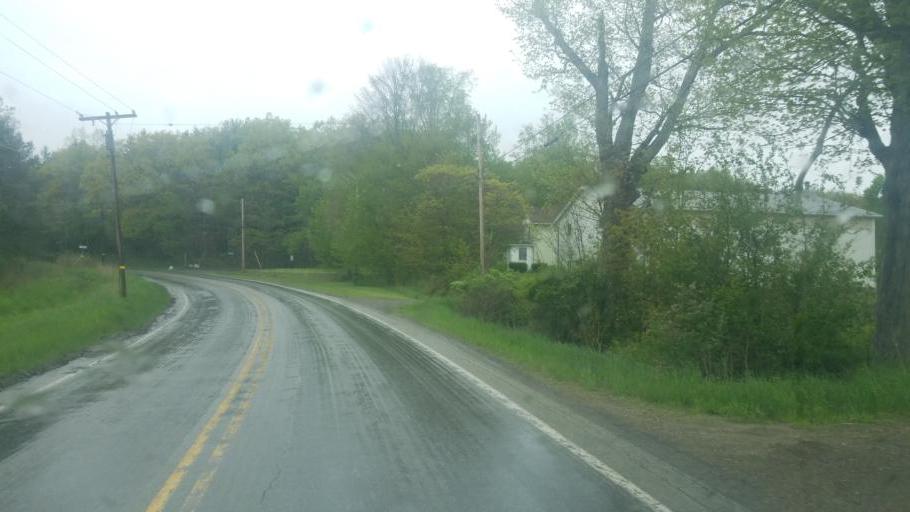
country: US
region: Pennsylvania
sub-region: Forest County
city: Tionesta
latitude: 41.3898
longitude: -79.3219
